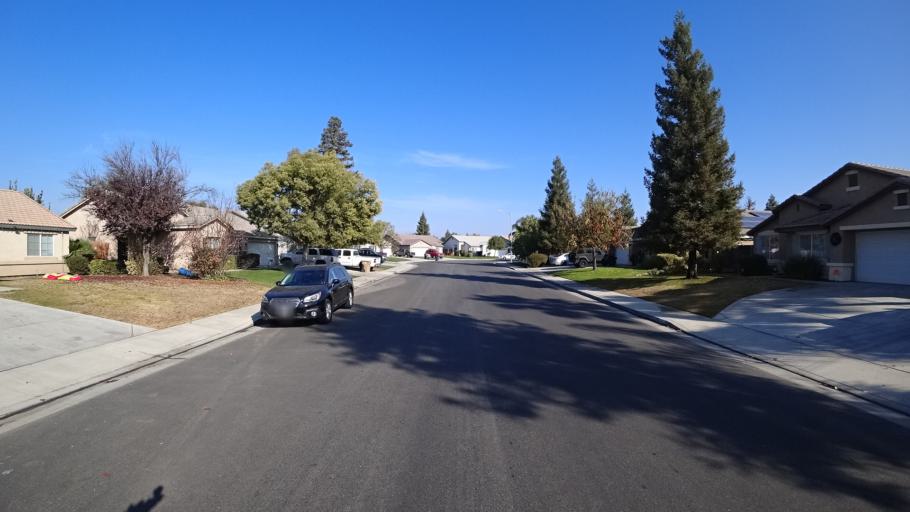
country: US
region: California
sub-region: Kern County
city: Greenacres
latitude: 35.3127
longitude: -119.1130
